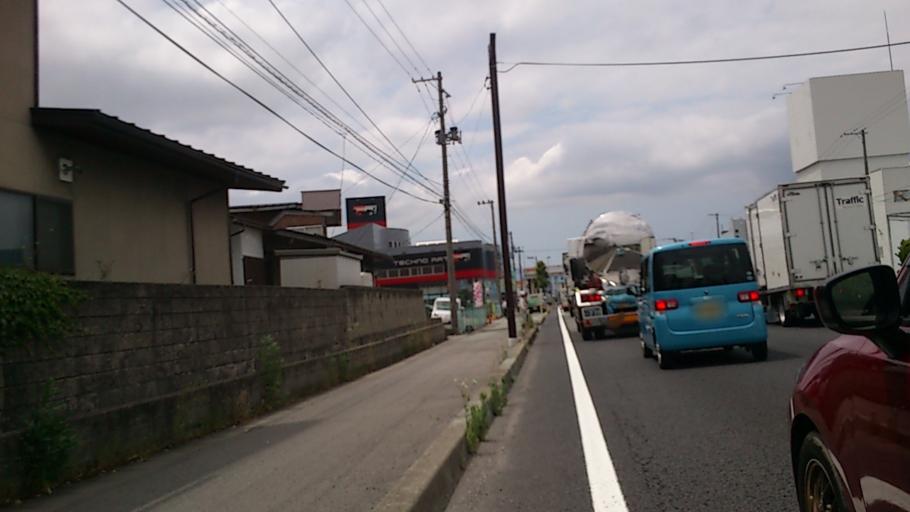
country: JP
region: Yamagata
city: Yamagata-shi
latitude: 38.2258
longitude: 140.3360
